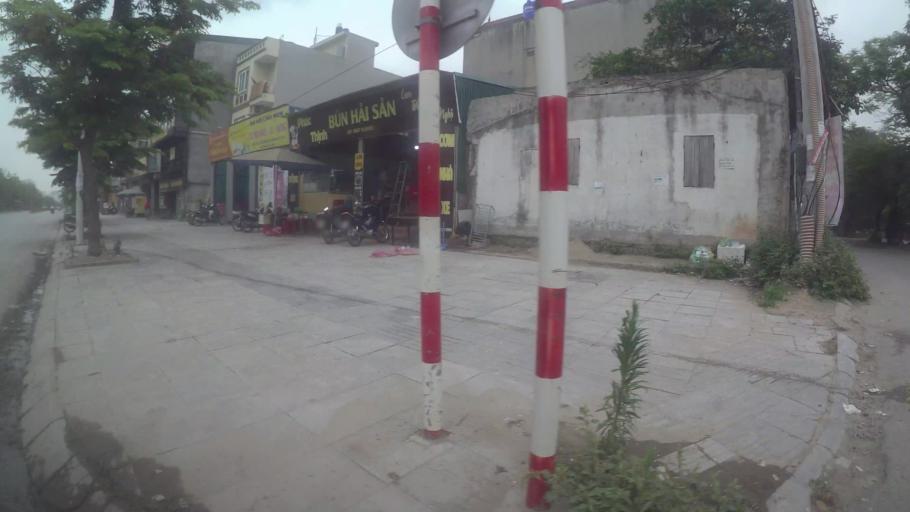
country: VN
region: Ha Noi
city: Cau Dien
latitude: 21.0391
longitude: 105.7427
